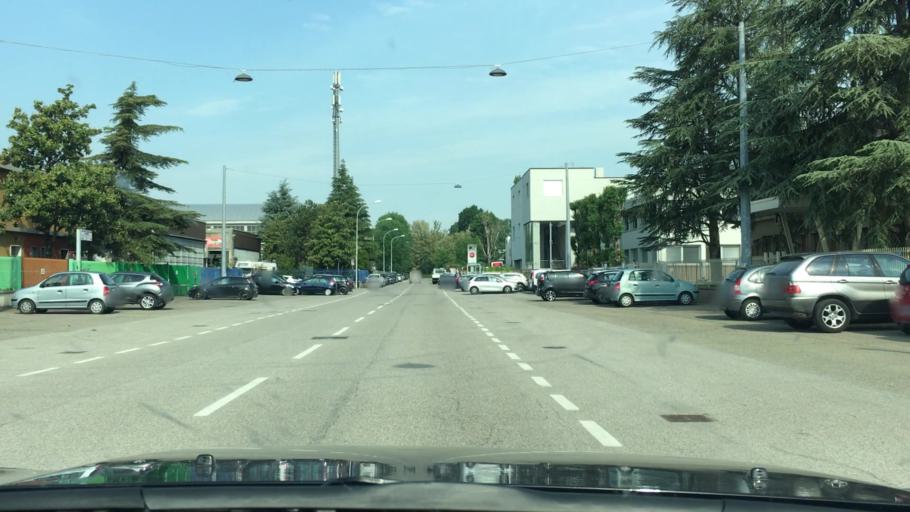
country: IT
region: Emilia-Romagna
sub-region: Provincia di Bologna
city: Quarto Inferiore
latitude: 44.5512
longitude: 11.3940
